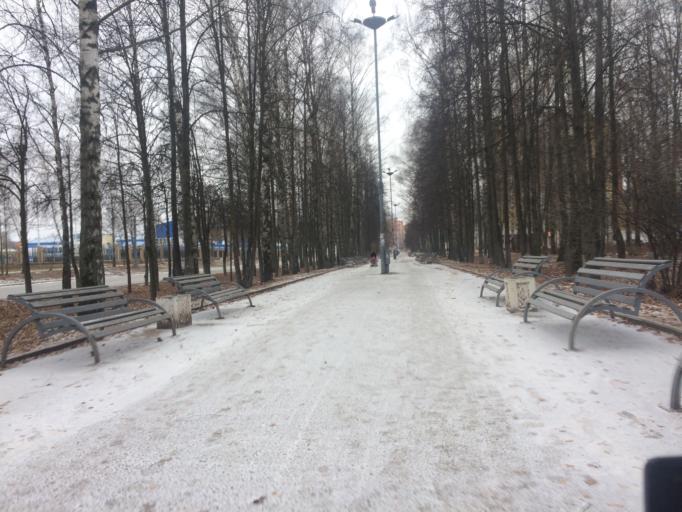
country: RU
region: Mariy-El
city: Yoshkar-Ola
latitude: 56.6437
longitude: 47.8733
